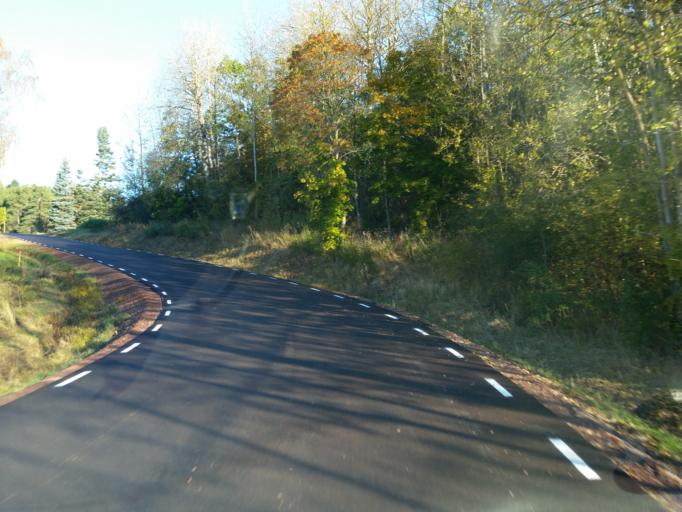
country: AX
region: Alands landsbygd
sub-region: Sund
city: Sund
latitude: 60.2263
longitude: 20.0919
